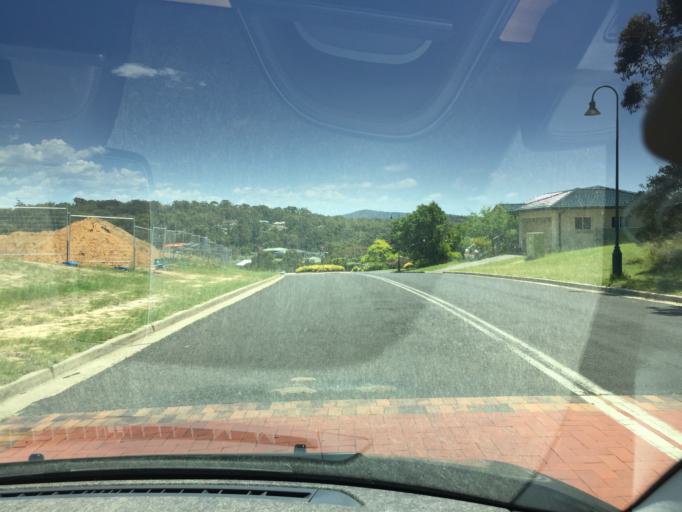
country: AU
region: New South Wales
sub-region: Bega Valley
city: Merimbula
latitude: -36.8516
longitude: 149.9318
